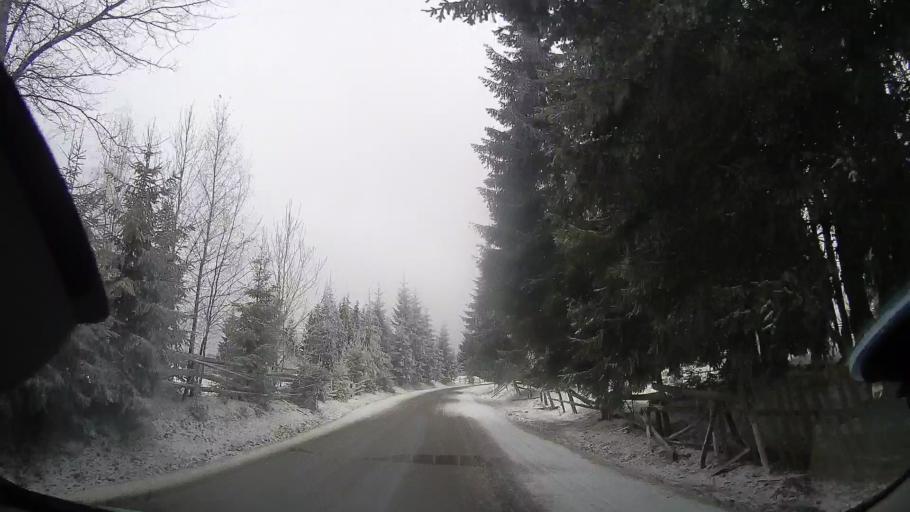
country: RO
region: Cluj
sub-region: Comuna Maguri-Racatau
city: Maguri
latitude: 46.6552
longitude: 23.0857
